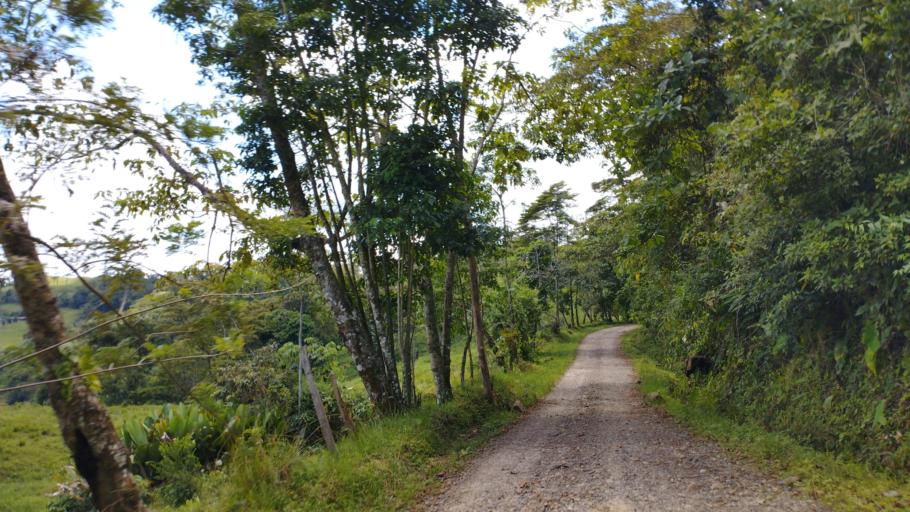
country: CO
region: Boyaca
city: San Luis de Gaceno
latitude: 4.7823
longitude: -73.1218
